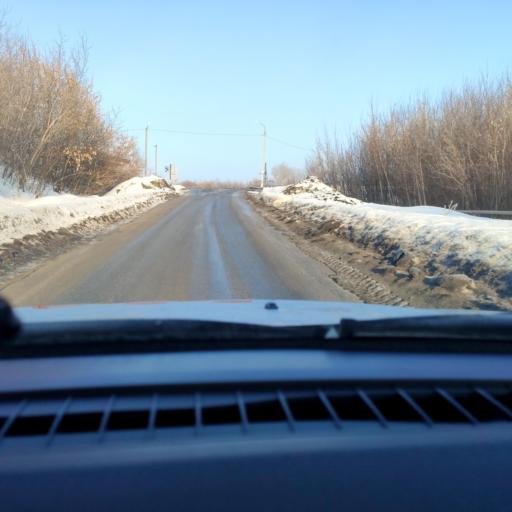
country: RU
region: Samara
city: Novokuybyshevsk
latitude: 53.1204
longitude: 49.9433
